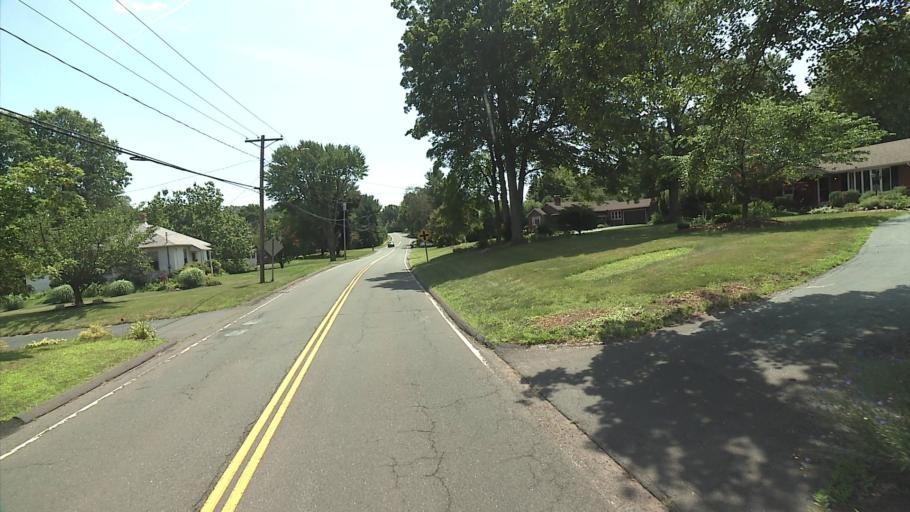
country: US
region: Connecticut
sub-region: Hartford County
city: Kensington
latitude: 41.6393
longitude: -72.7776
